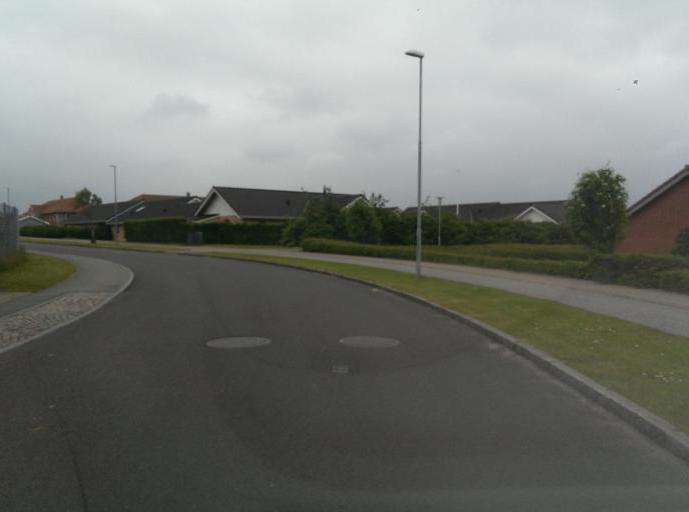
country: DK
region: South Denmark
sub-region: Fano Kommune
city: Nordby
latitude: 55.5333
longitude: 8.3558
